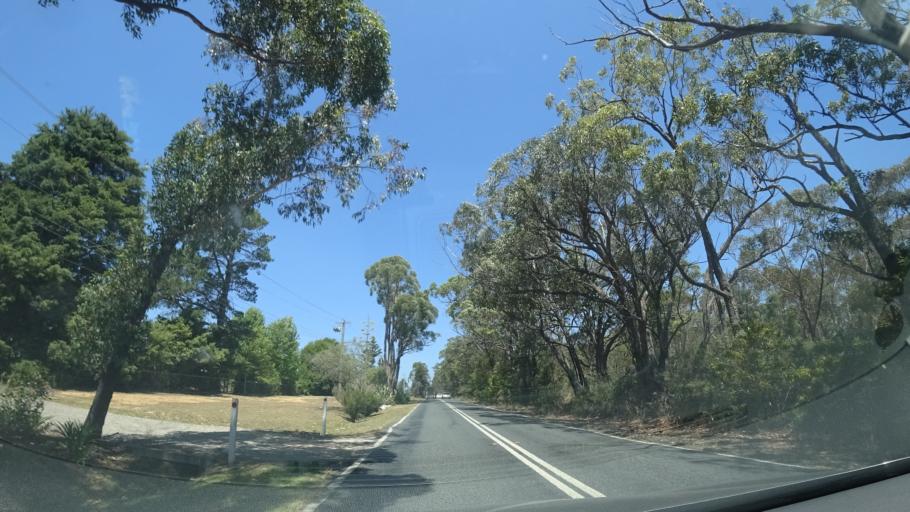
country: AU
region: New South Wales
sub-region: Wingecarribee
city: Colo Vale
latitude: -34.3482
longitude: 150.4935
